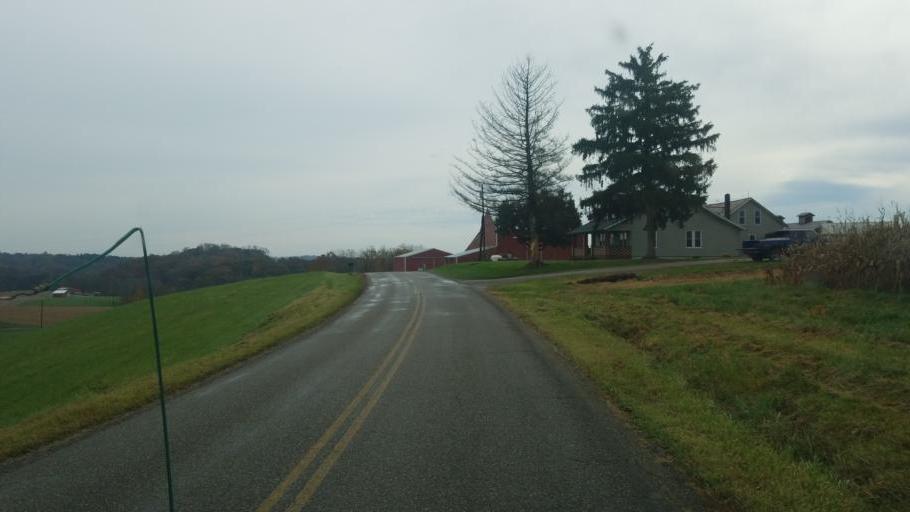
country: US
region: Ohio
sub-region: Washington County
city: Beverly
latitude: 39.5538
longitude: -81.6882
